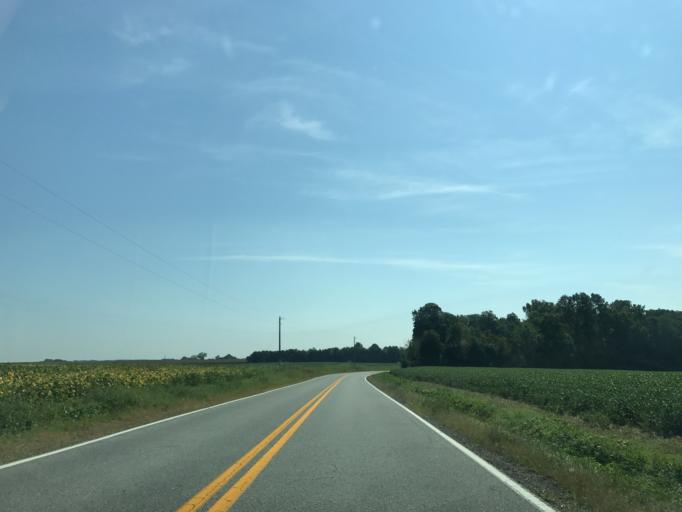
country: US
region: Maryland
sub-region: Queen Anne's County
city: Kingstown
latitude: 39.3020
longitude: -75.9616
